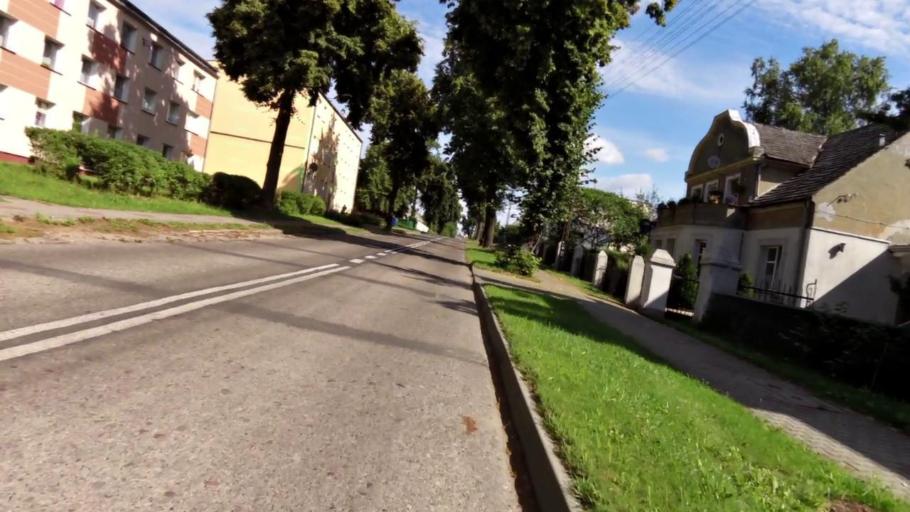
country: PL
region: West Pomeranian Voivodeship
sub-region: Powiat stargardzki
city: Dobrzany
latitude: 53.3621
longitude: 15.4285
